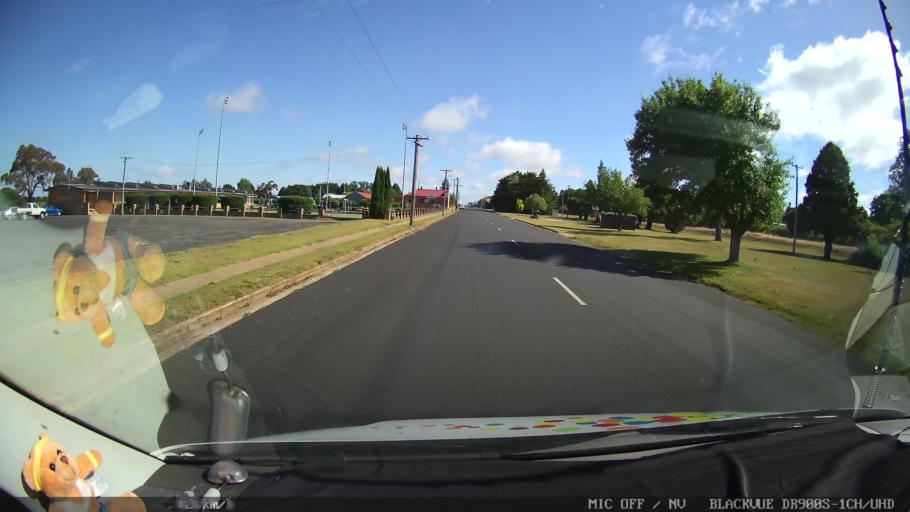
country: AU
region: New South Wales
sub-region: Guyra
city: Guyra
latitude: -30.2252
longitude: 151.6709
